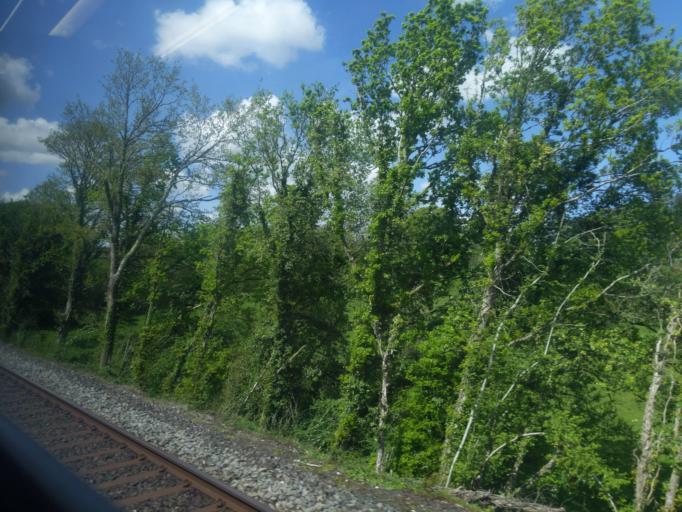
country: GB
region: England
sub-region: Cornwall
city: Pillaton
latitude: 50.4195
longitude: -4.3761
